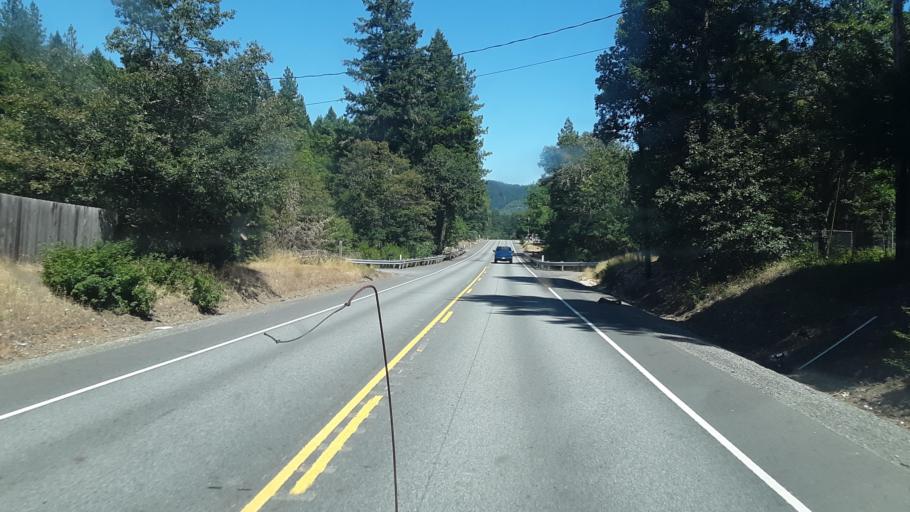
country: US
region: Oregon
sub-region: Josephine County
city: Redwood
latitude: 42.3641
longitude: -123.5342
